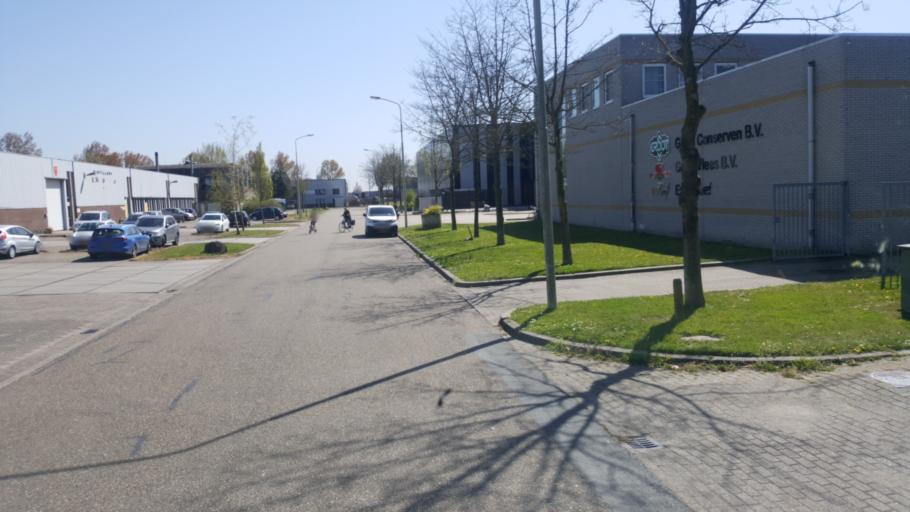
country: NL
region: North Holland
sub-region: Gemeente Hoorn
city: Hoorn
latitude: 52.6390
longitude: 5.1024
